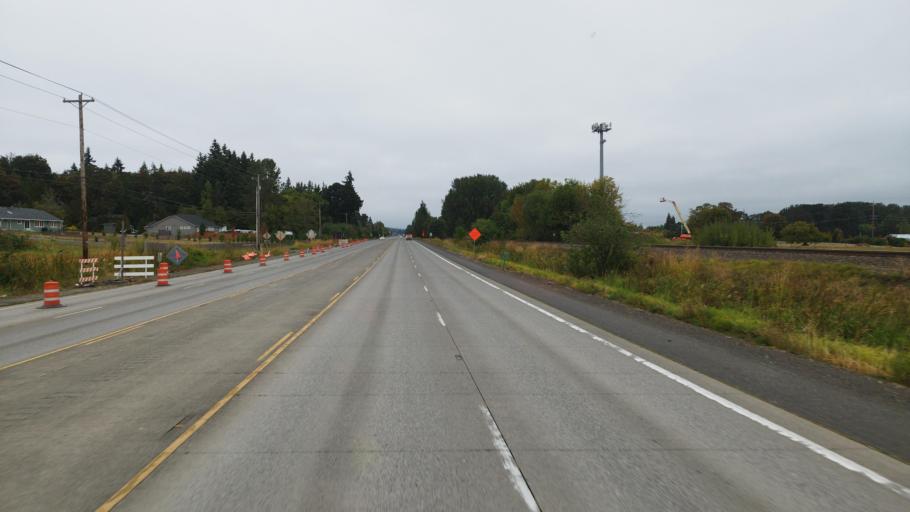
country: US
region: Oregon
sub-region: Columbia County
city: Warren
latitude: 45.8250
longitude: -122.8451
